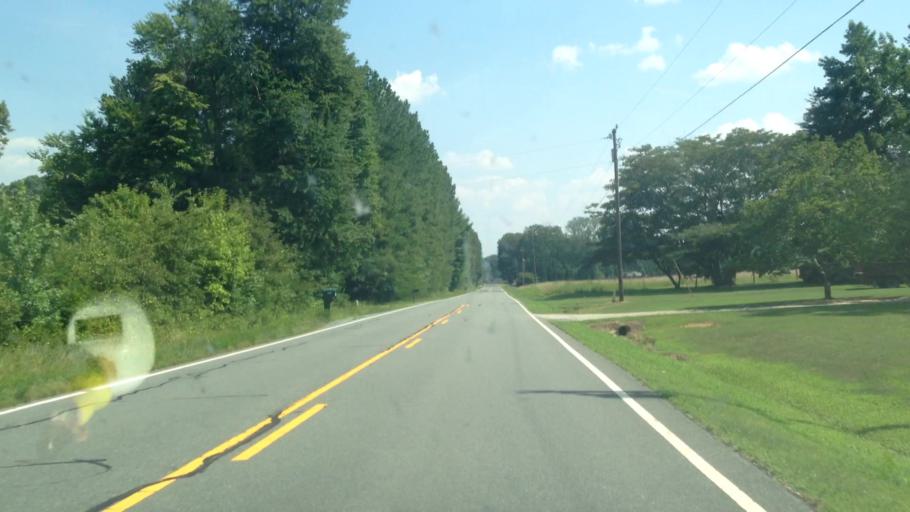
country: US
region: North Carolina
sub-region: Rockingham County
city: Madison
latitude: 36.3466
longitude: -80.0536
